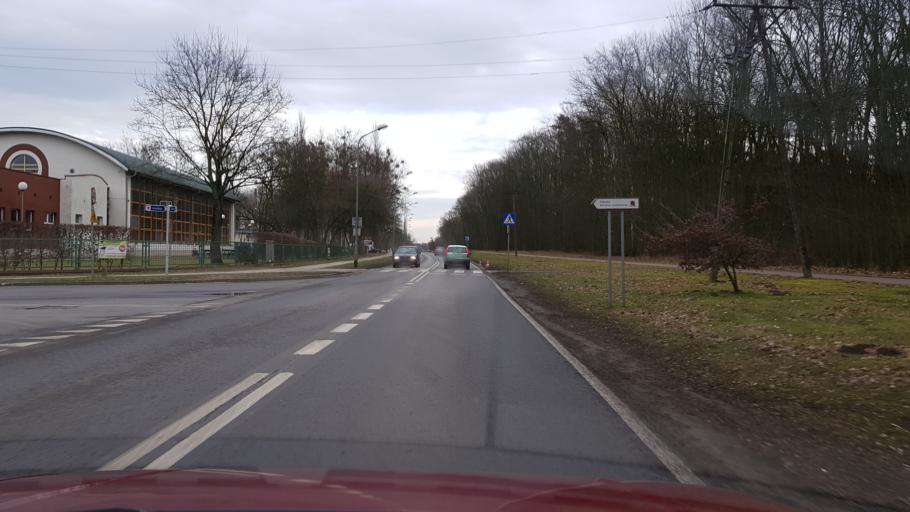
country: PL
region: West Pomeranian Voivodeship
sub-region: Powiat policki
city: Police
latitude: 53.5511
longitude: 14.5416
